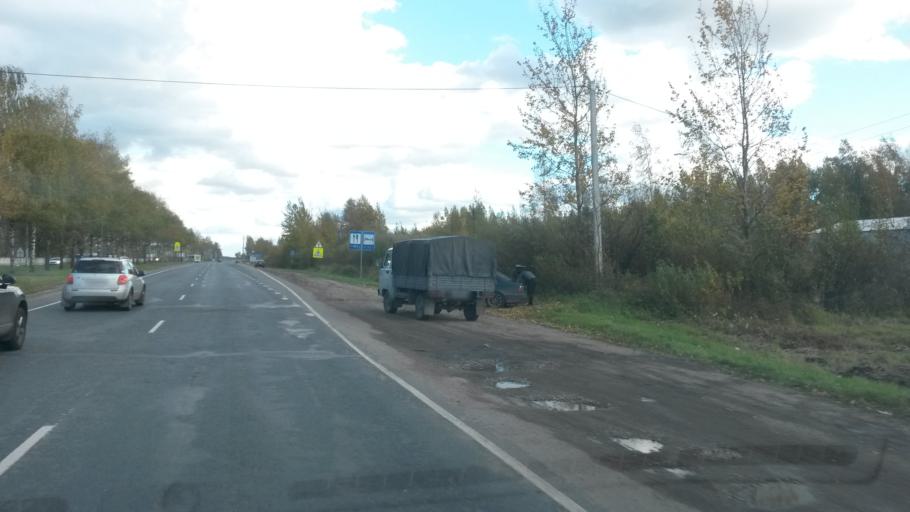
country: RU
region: Jaroslavl
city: Yaroslavl
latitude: 57.5411
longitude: 39.9739
